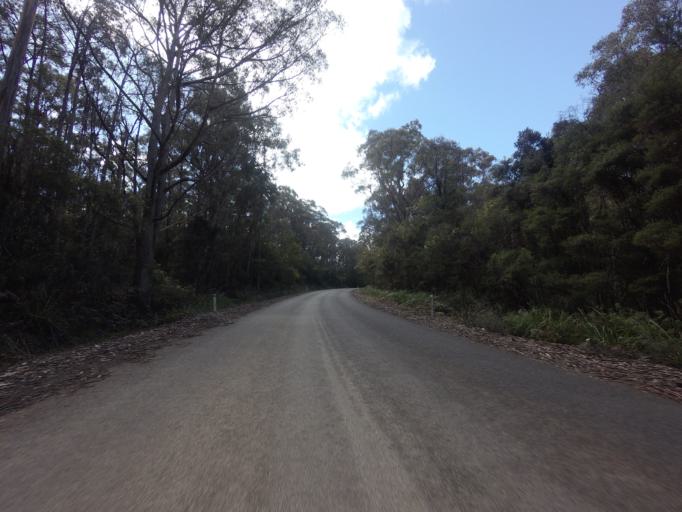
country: AU
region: Tasmania
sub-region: Huon Valley
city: Geeveston
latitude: -43.4147
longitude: 146.9102
